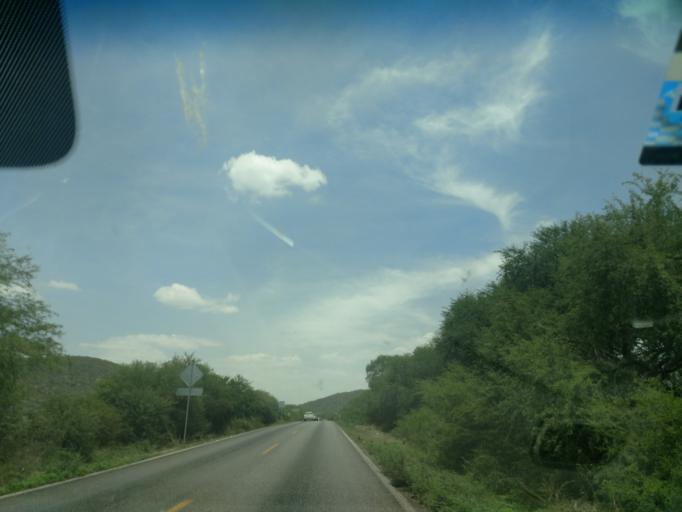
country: MX
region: San Luis Potosi
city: Ciudad Fernandez
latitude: 22.0030
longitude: -100.1449
